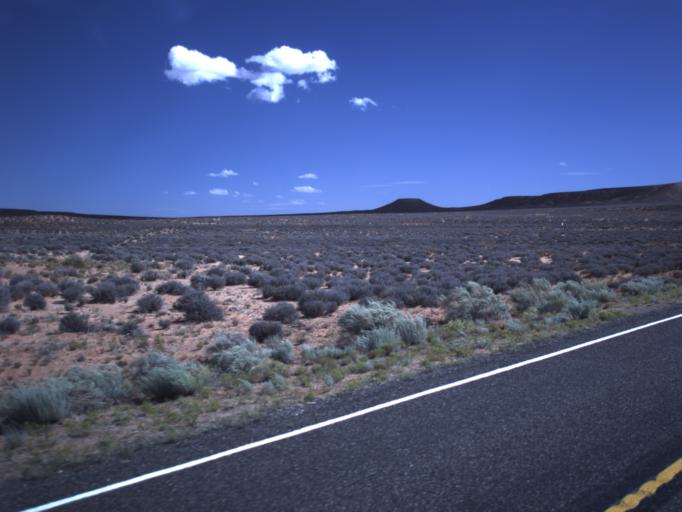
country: US
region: Utah
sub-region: Wayne County
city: Loa
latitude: 38.1608
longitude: -110.6221
